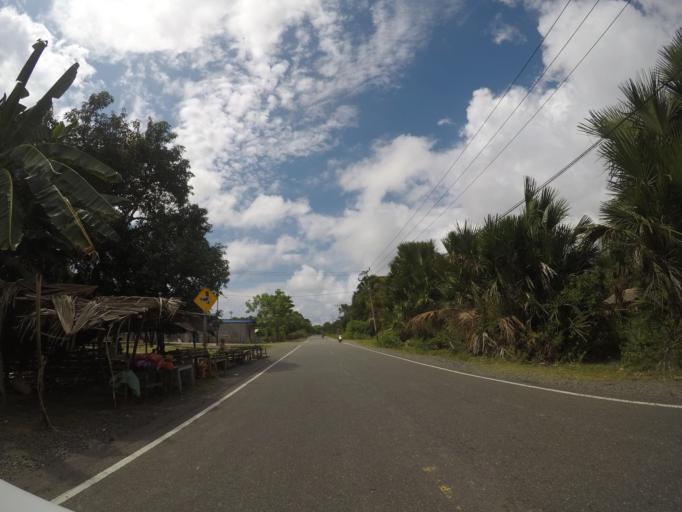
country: TL
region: Liquica
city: Maubara
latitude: -8.7245
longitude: 125.1123
